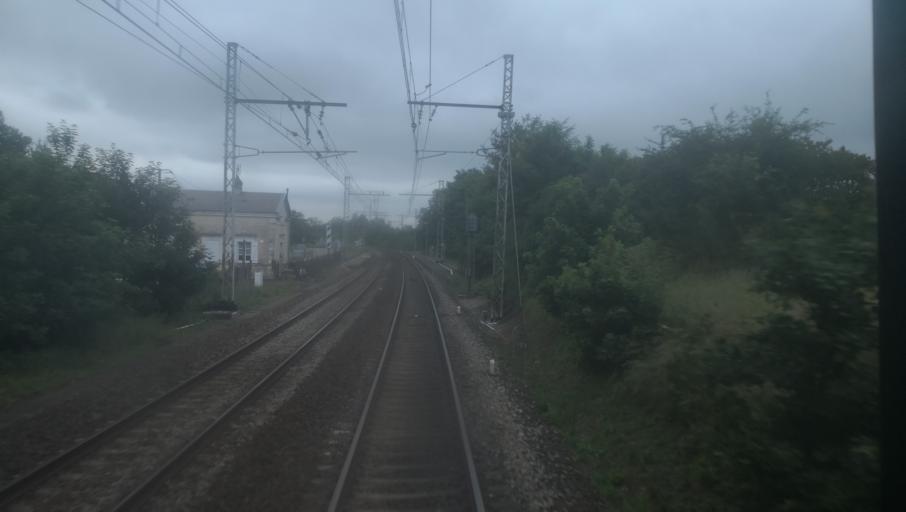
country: FR
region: Centre
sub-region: Departement de l'Indre
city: Sainte-Lizaigne
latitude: 47.0019
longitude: 2.0299
